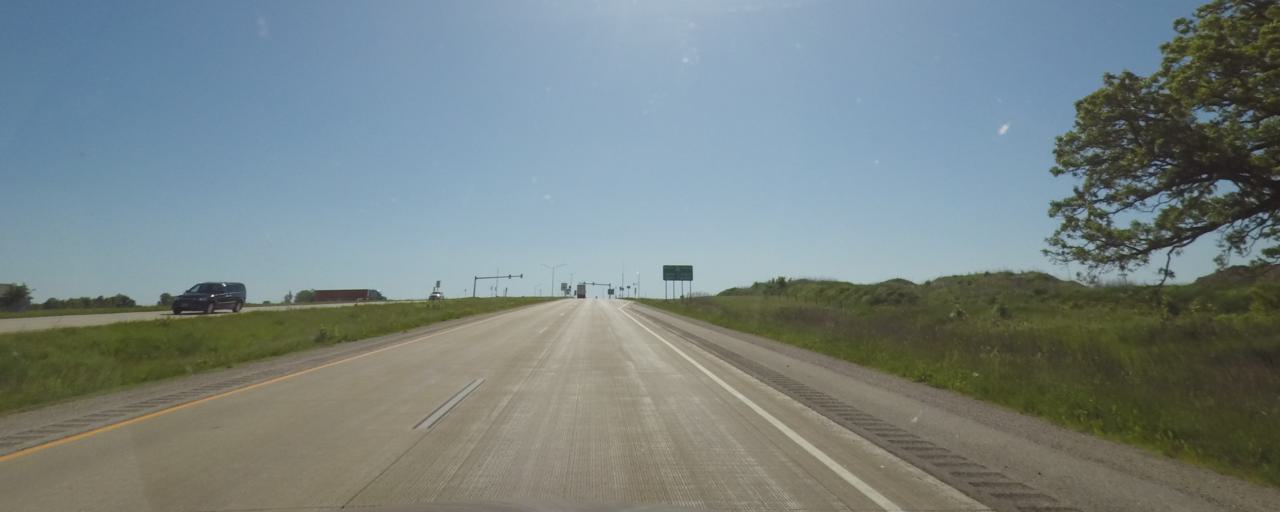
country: US
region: Wisconsin
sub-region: Fond du Lac County
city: Fond du Lac
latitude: 43.7373
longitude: -88.4493
